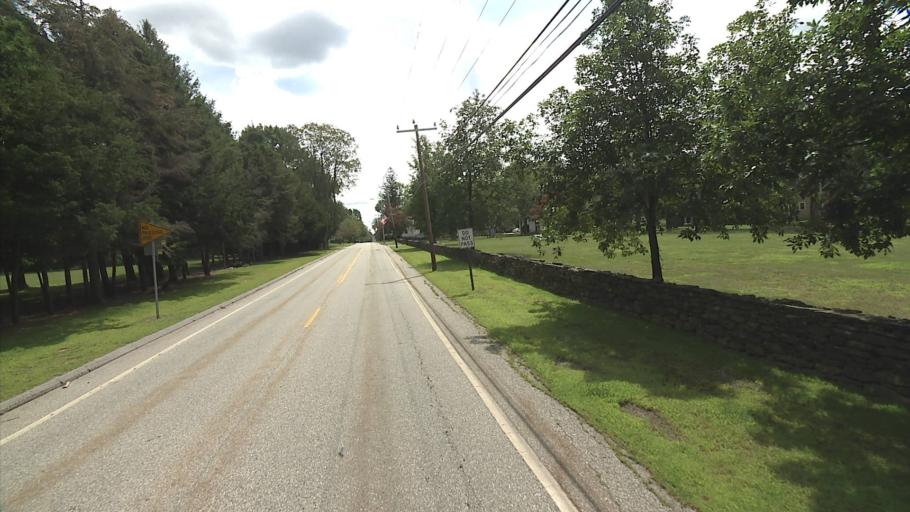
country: US
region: Connecticut
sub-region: Windham County
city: Thompson
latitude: 41.9616
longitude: -71.8667
